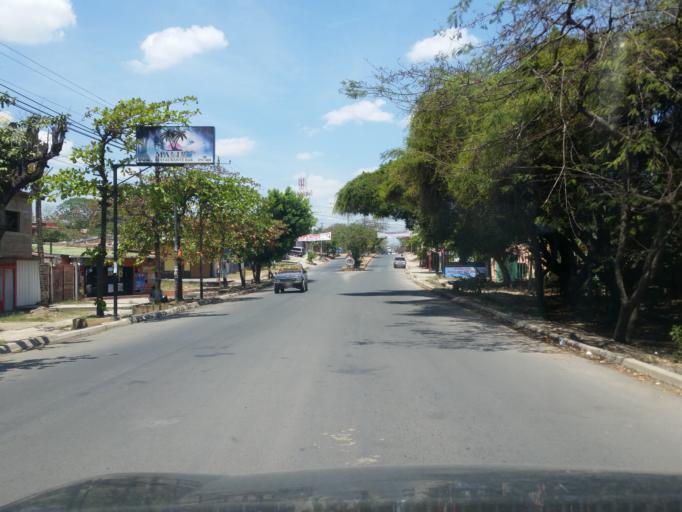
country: NI
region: Esteli
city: Esteli
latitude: 13.0729
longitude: -86.3527
